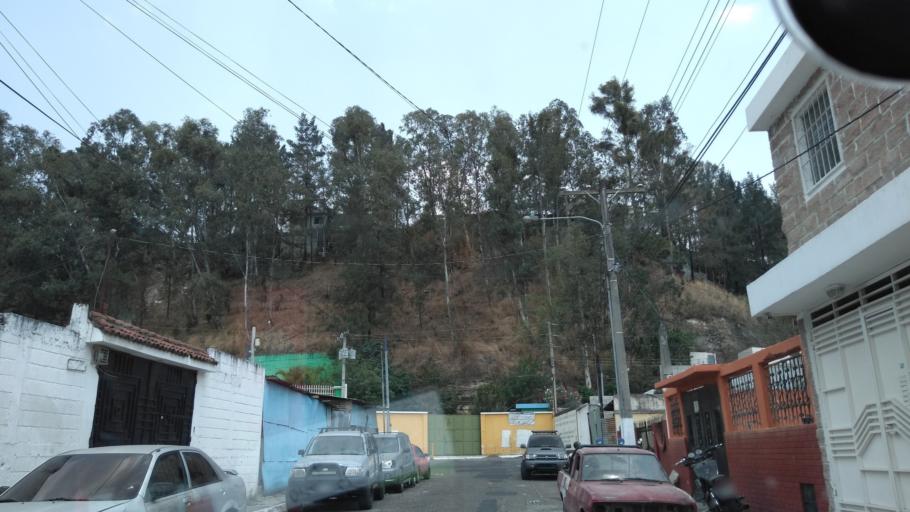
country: GT
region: Guatemala
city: Petapa
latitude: 14.5239
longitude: -90.5425
